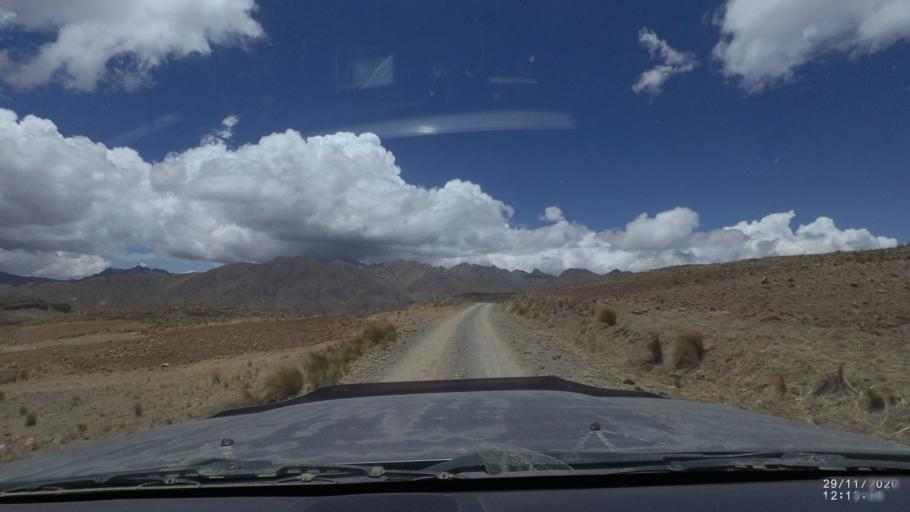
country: BO
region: Cochabamba
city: Cochabamba
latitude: -17.1098
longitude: -66.3054
